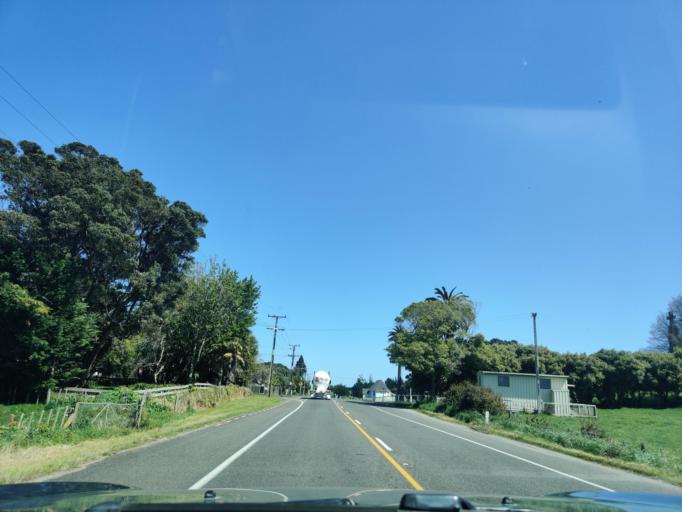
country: NZ
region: Manawatu-Wanganui
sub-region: Wanganui District
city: Wanganui
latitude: -39.8211
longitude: 174.8640
